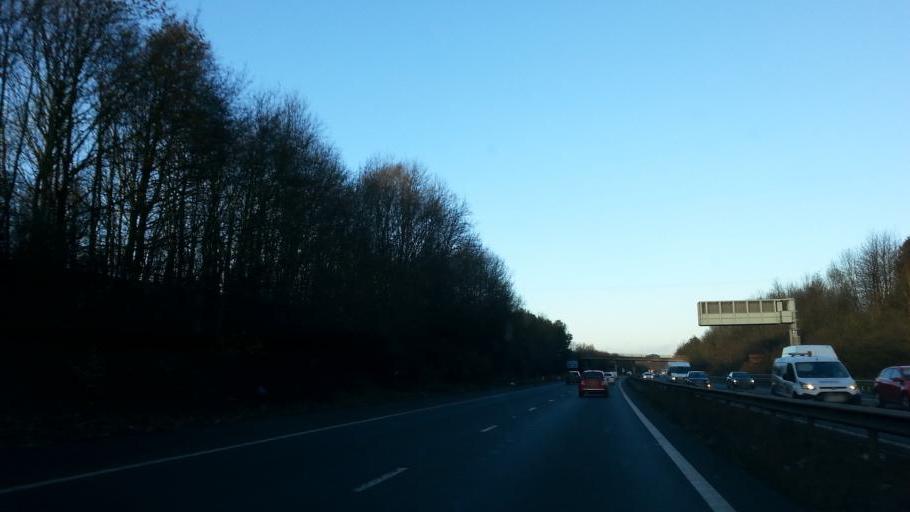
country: GB
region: England
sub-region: Staffordshire
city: Tamworth
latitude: 52.6167
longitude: -1.6322
